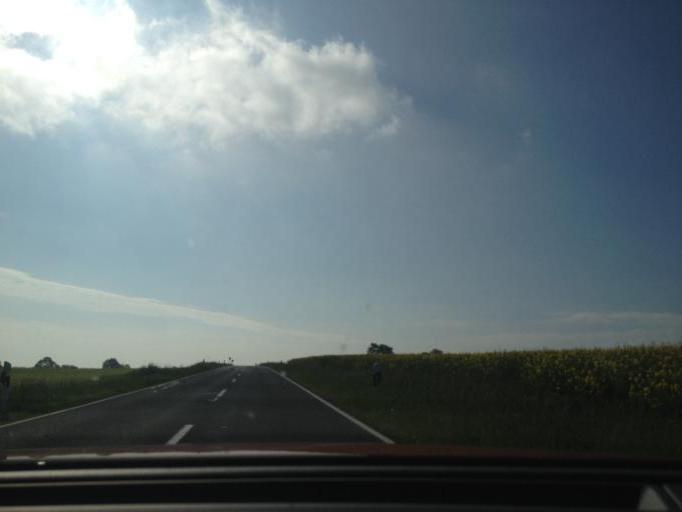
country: DE
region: Bavaria
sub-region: Upper Palatinate
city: Kirchenthumbach
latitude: 49.7626
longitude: 11.6886
